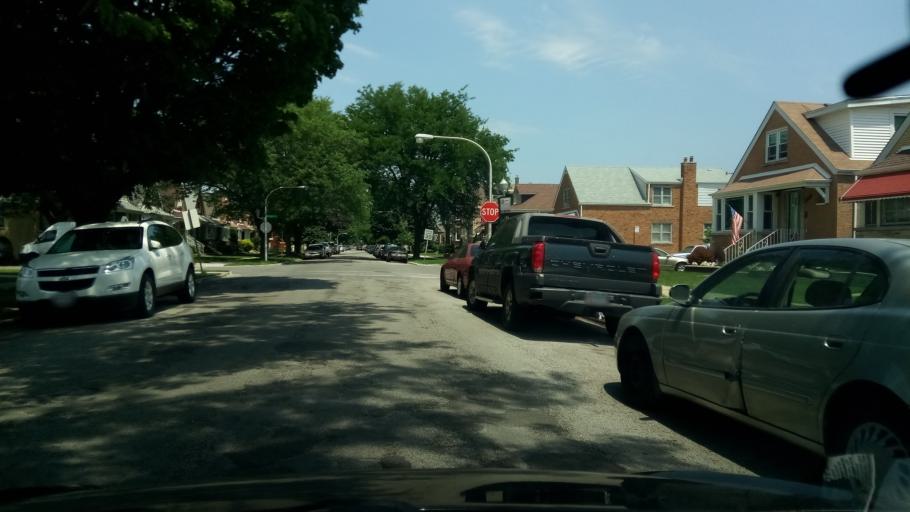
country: US
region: Illinois
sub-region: Cook County
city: Hometown
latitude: 41.7800
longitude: -87.7326
